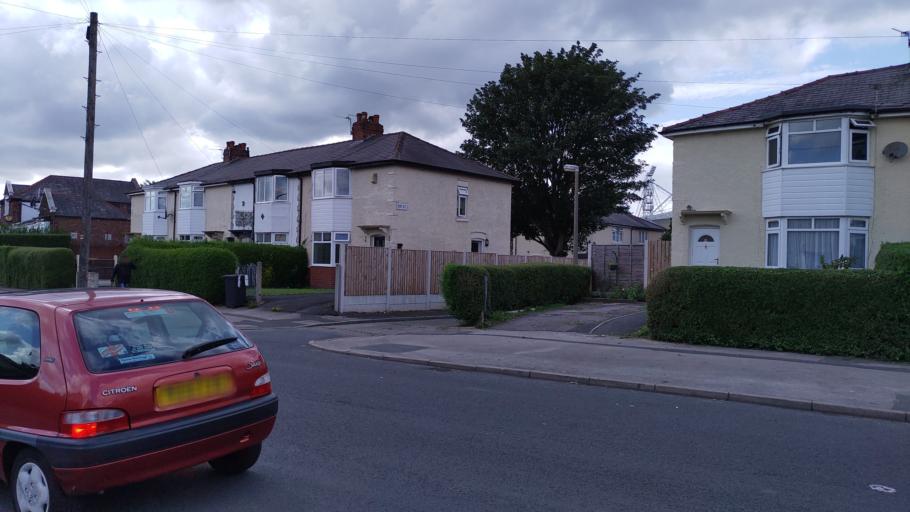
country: GB
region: England
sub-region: Lancashire
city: Preston
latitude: 53.7706
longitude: -2.6839
